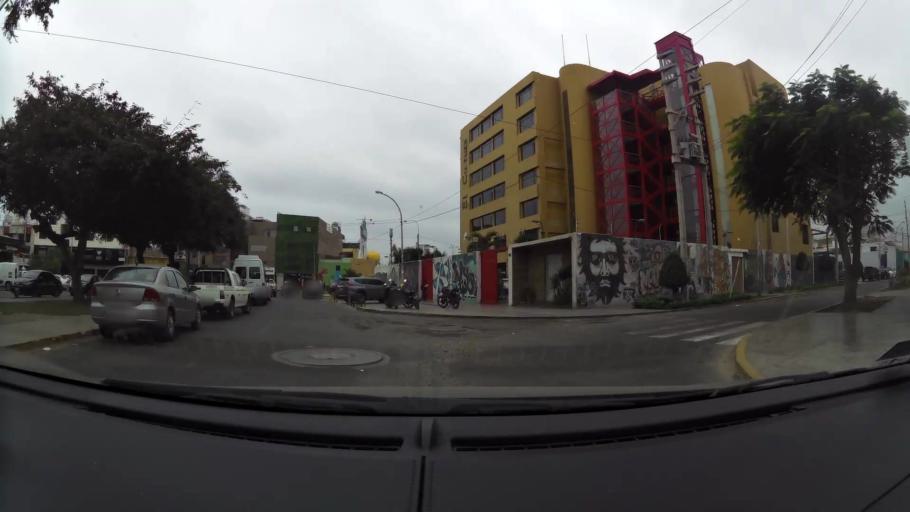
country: PE
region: La Libertad
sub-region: Provincia de Trujillo
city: Trujillo
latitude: -8.1186
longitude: -79.0322
